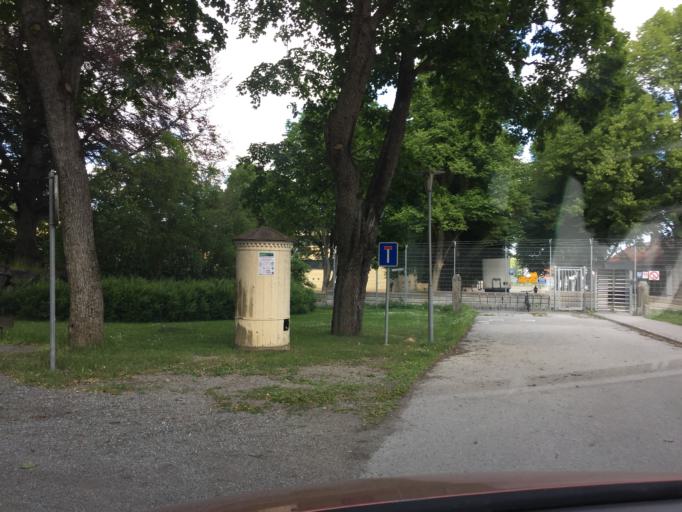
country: SE
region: Stockholm
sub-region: Botkyrka Kommun
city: Tumba
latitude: 59.2013
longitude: 17.8224
